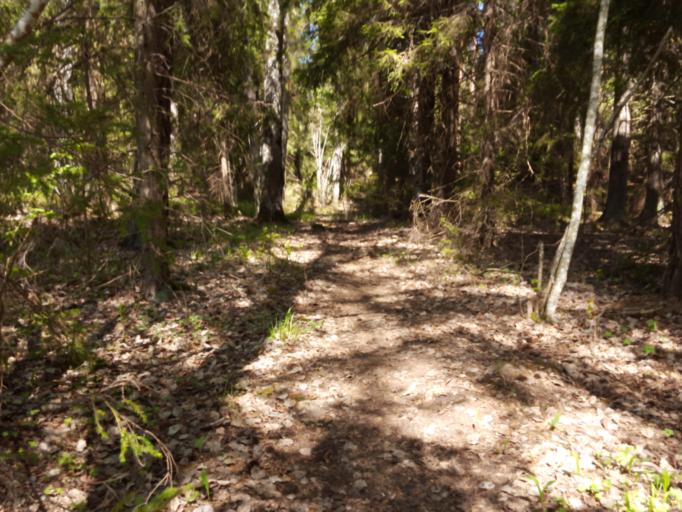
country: SE
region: Uppsala
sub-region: Uppsala Kommun
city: Storvreta
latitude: 59.9019
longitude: 17.7426
